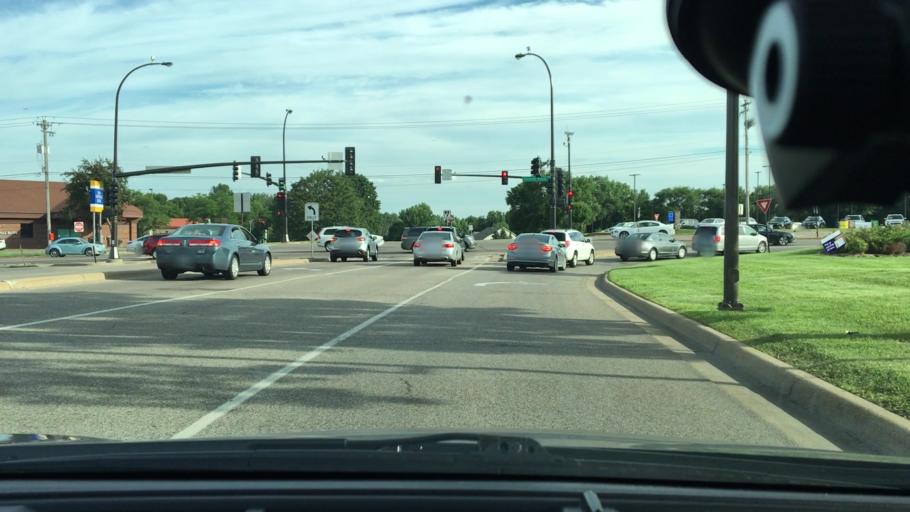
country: US
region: Minnesota
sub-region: Hennepin County
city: Plymouth
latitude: 45.0286
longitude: -93.4489
